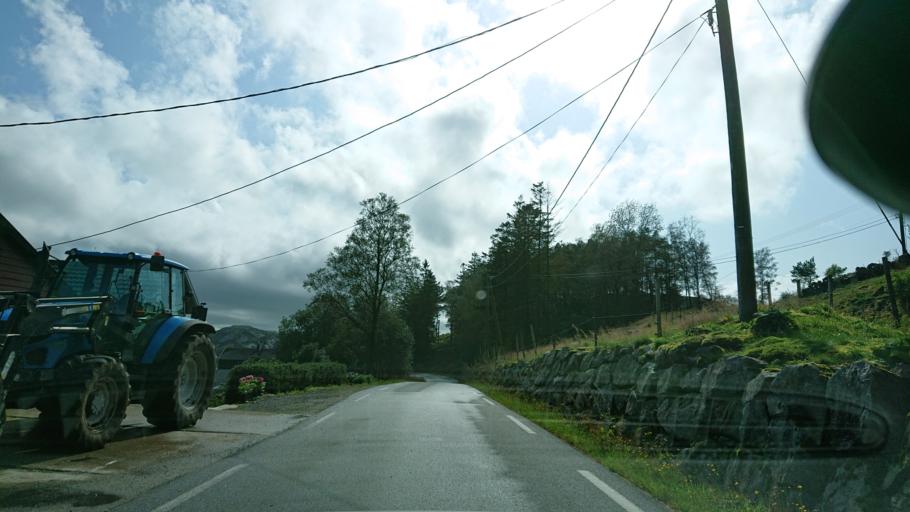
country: NO
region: Rogaland
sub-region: Gjesdal
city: Algard
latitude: 58.6955
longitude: 5.8838
